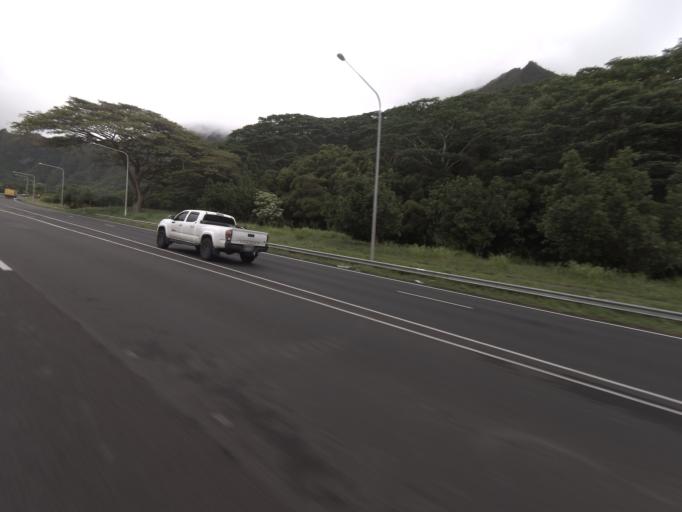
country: US
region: Hawaii
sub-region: Honolulu County
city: Kane'ohe
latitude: 21.3971
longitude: -157.8105
